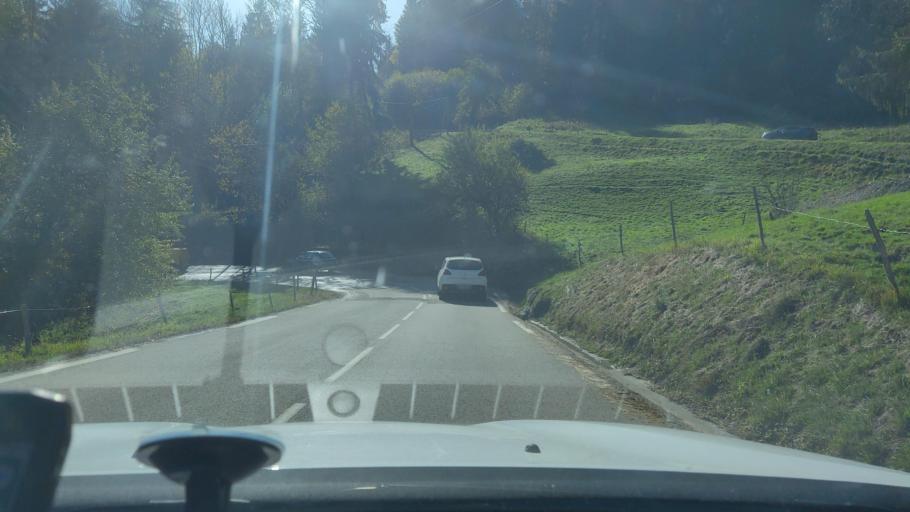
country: FR
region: Rhone-Alpes
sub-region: Departement de la Savoie
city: Ugine
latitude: 45.7931
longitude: 6.4827
